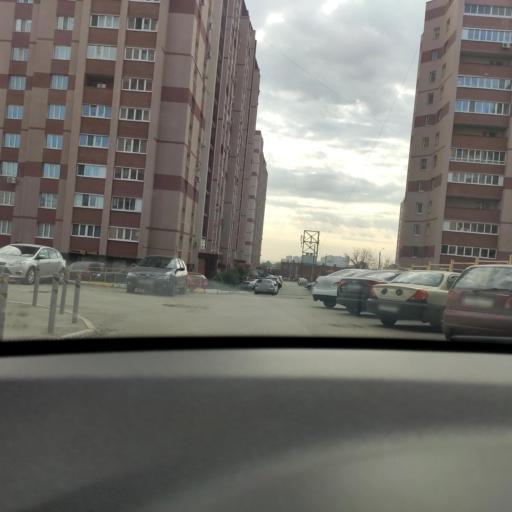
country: RU
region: Samara
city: Samara
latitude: 53.2089
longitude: 50.2075
